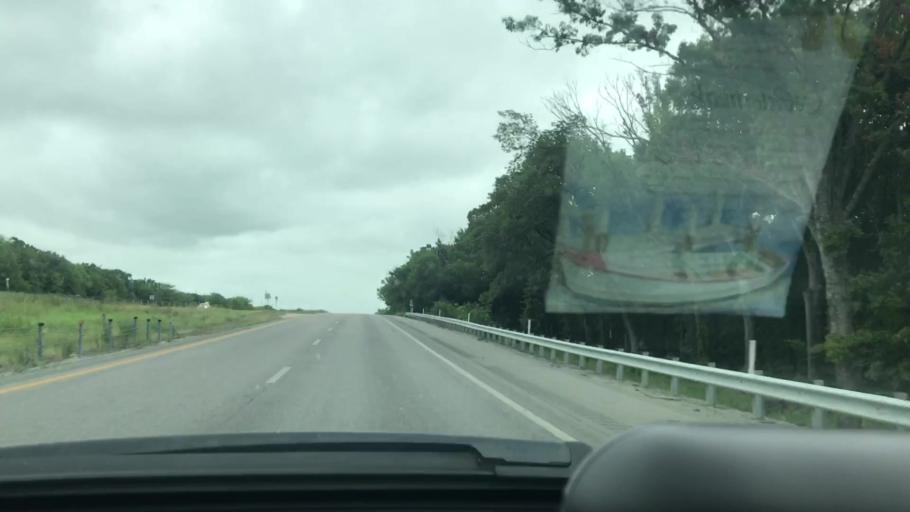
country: US
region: Oklahoma
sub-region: Coal County
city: Coalgate
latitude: 34.6284
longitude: -95.9587
